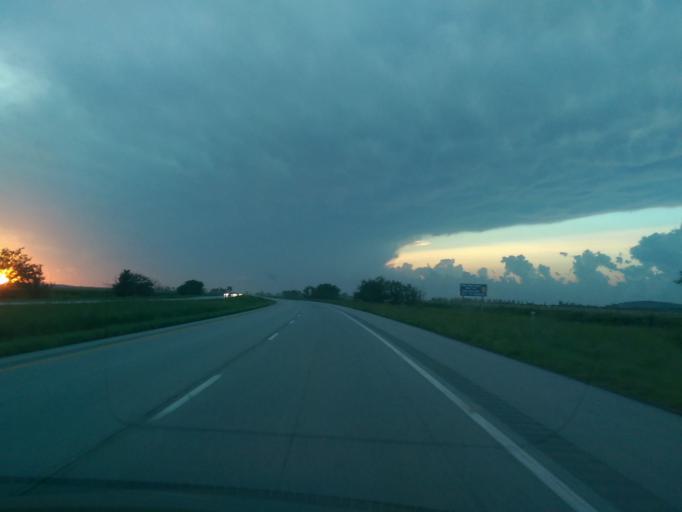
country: US
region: Iowa
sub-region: Fremont County
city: Hamburg
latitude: 40.6070
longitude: -95.6834
